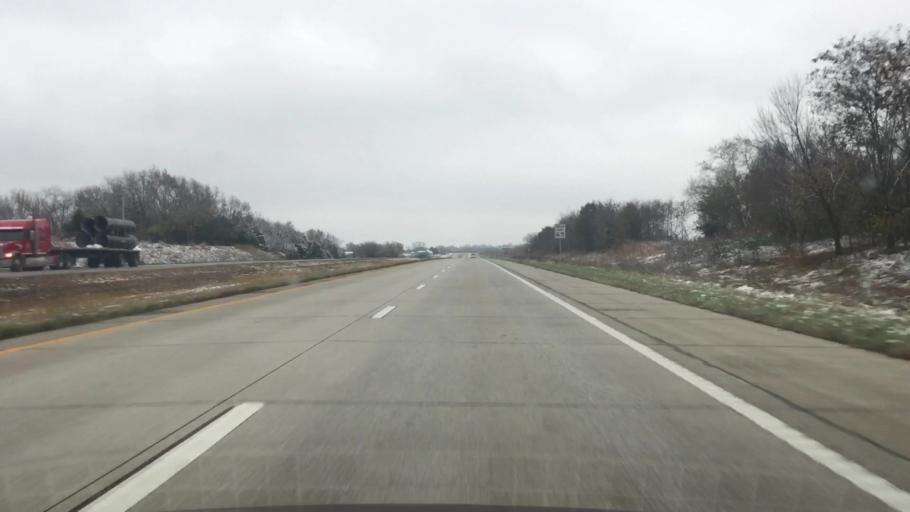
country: US
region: Missouri
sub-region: Saint Clair County
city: Osceola
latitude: 38.2036
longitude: -93.7512
